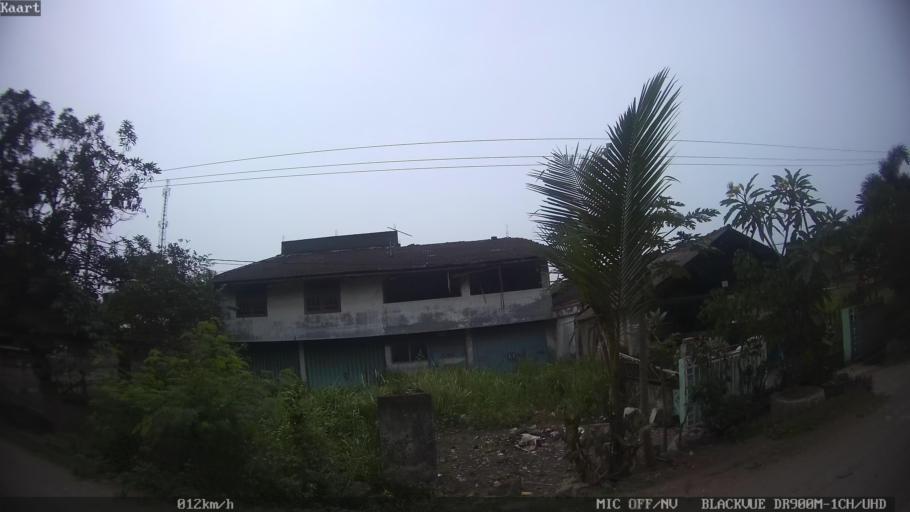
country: ID
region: Lampung
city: Panjang
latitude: -5.4401
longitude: 105.3178
